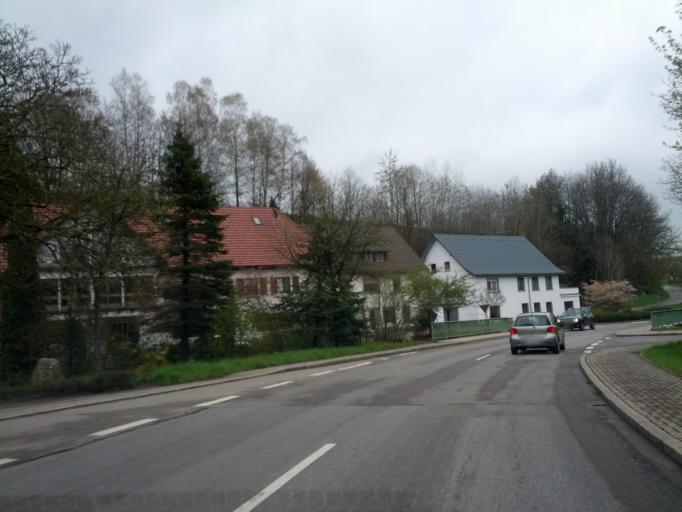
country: DE
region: Baden-Wuerttemberg
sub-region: Freiburg Region
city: Rickenbach
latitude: 47.6254
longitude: 8.0045
